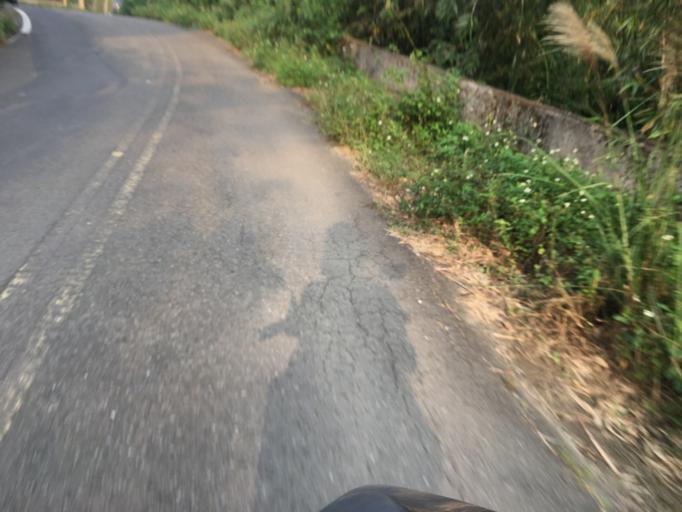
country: TW
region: Taiwan
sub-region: Hsinchu
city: Hsinchu
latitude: 24.7106
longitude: 121.0589
